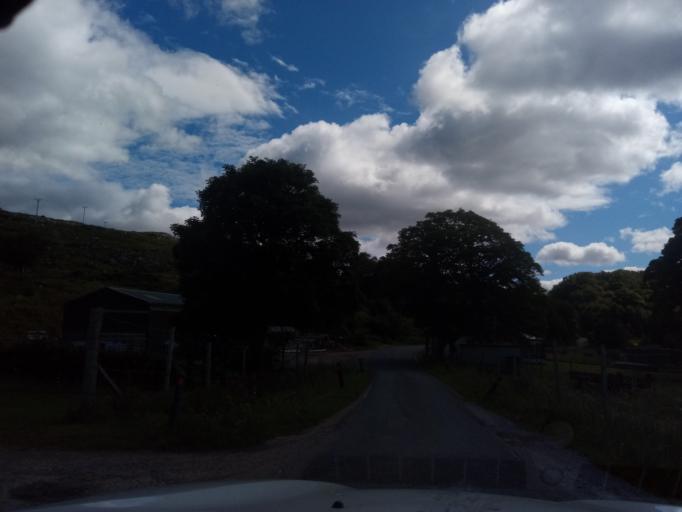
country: GB
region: Scotland
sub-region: Argyll and Bute
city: Isle Of Mull
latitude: 56.7630
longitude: -5.7489
